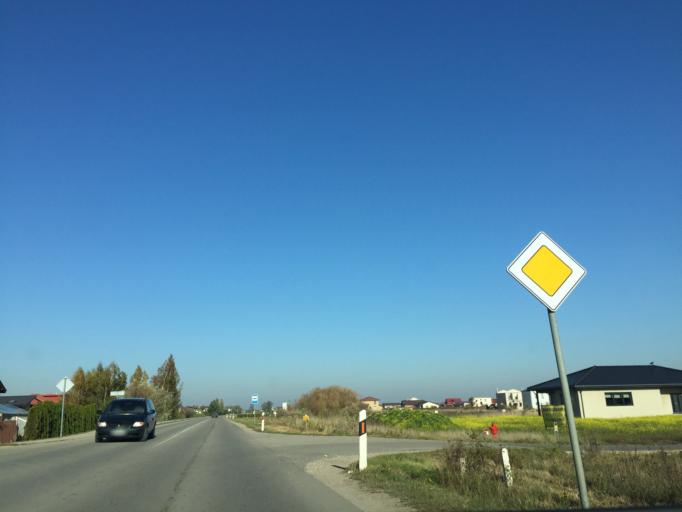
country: LT
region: Klaipedos apskritis
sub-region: Klaipeda
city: Klaipeda
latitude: 55.7420
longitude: 21.1924
